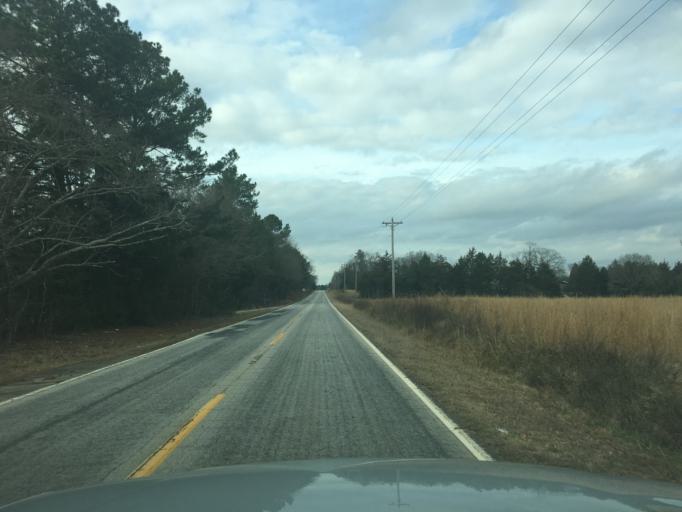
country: US
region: South Carolina
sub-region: Abbeville County
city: Due West
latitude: 34.3032
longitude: -82.4540
